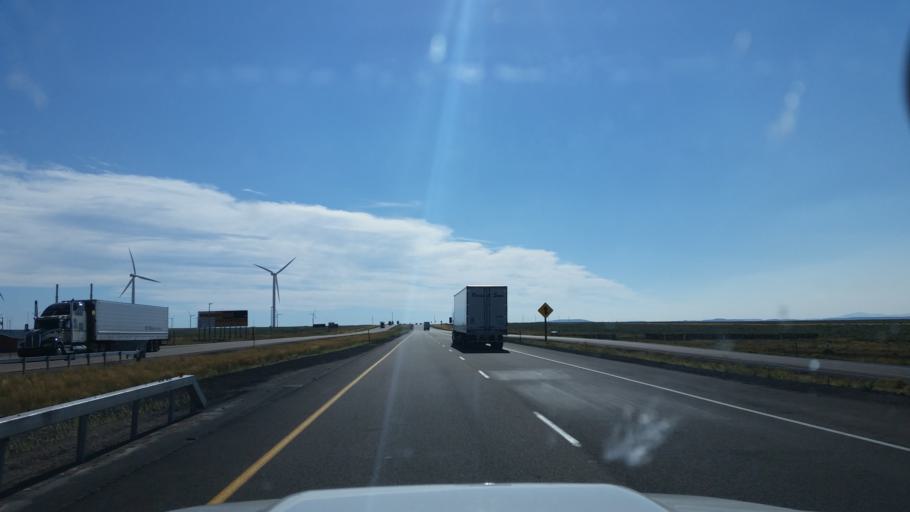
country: US
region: Wyoming
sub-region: Uinta County
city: Mountain View
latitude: 41.3127
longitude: -110.5089
